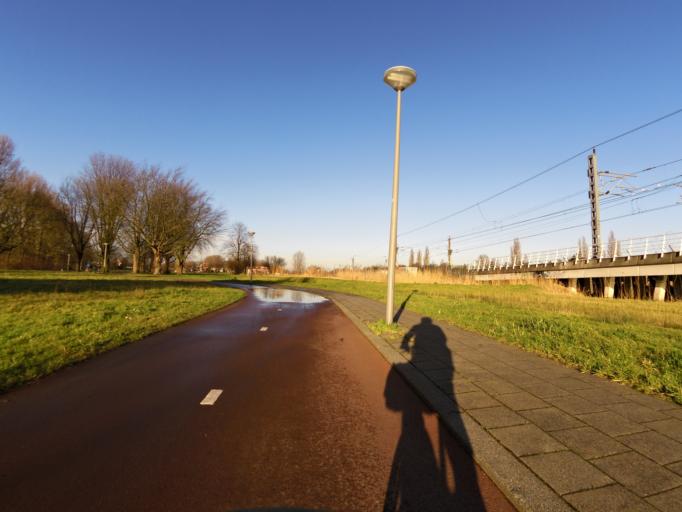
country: NL
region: South Holland
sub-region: Gemeente Rotterdam
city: Delfshaven
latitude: 51.9367
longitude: 4.4503
